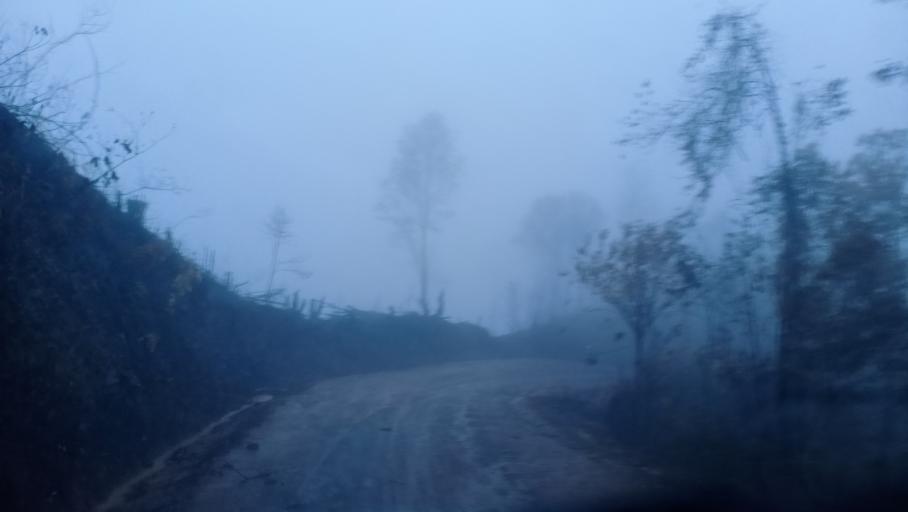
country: LA
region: Phongsali
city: Khoa
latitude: 21.2138
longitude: 102.2135
